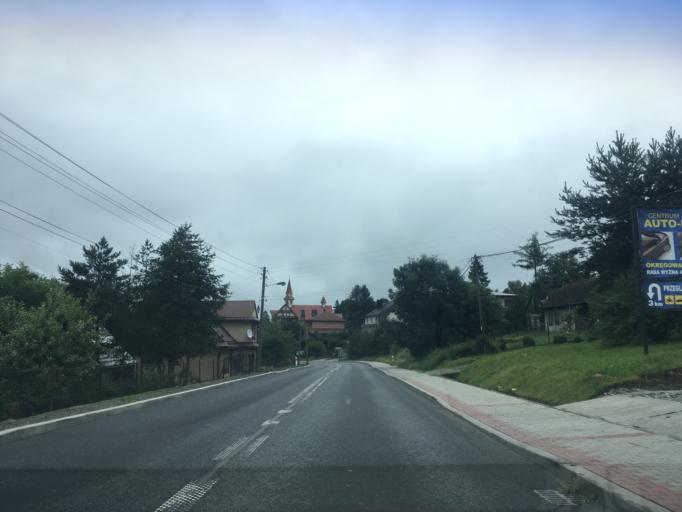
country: PL
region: Lesser Poland Voivodeship
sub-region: Powiat nowotarski
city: Rokiciny
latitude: 49.5918
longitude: 19.9246
